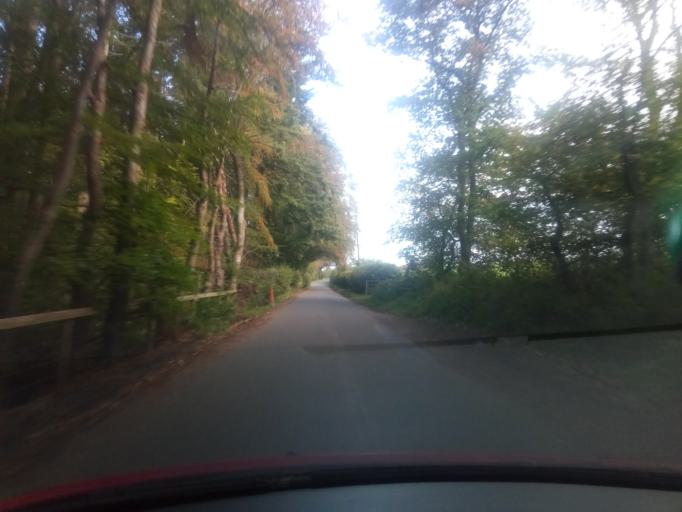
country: GB
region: Scotland
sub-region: The Scottish Borders
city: Jedburgh
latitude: 55.3775
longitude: -2.6475
